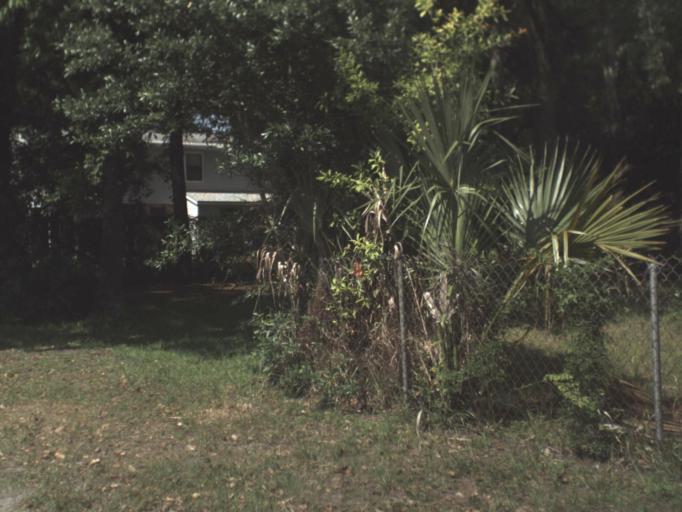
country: US
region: Florida
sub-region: Duval County
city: Jacksonville
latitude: 30.3588
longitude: -81.6412
